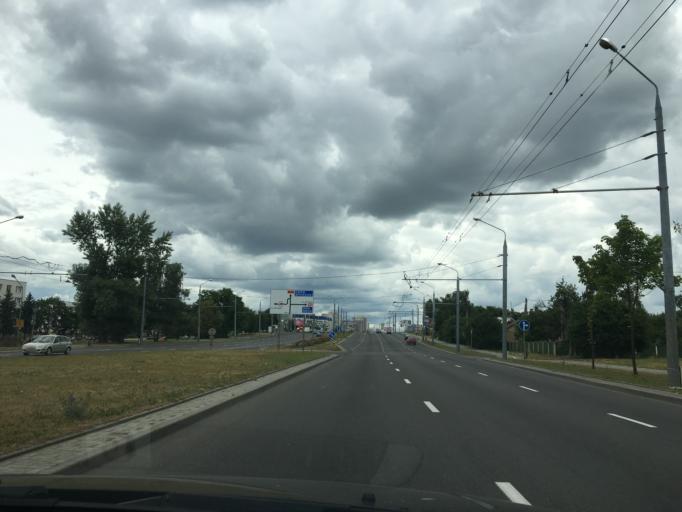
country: BY
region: Grodnenskaya
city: Hrodna
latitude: 53.6679
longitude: 23.8611
